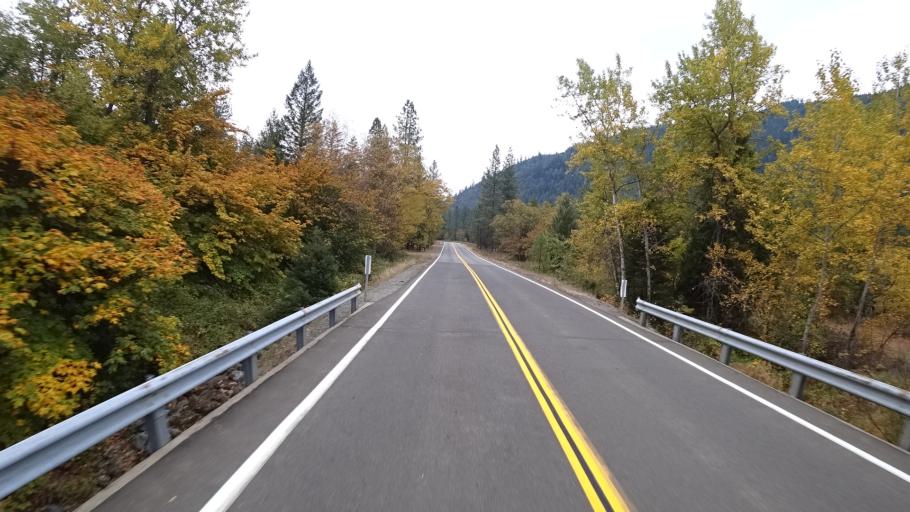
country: US
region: California
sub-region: Siskiyou County
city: Happy Camp
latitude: 41.8796
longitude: -123.4206
